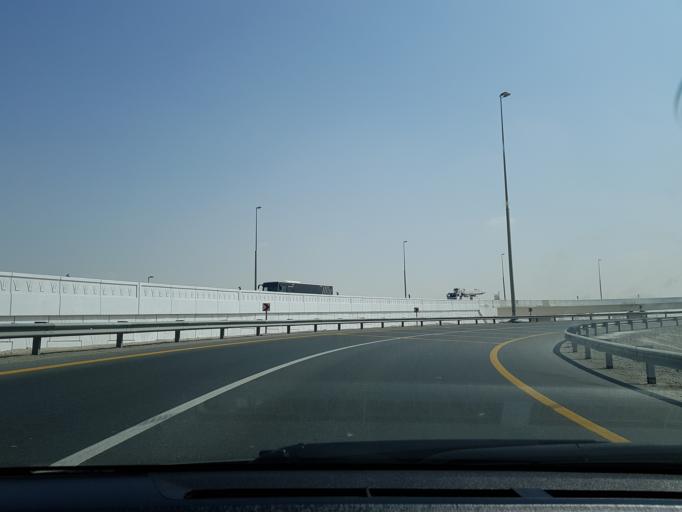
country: AE
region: Dubai
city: Dubai
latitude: 25.1453
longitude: 55.2624
